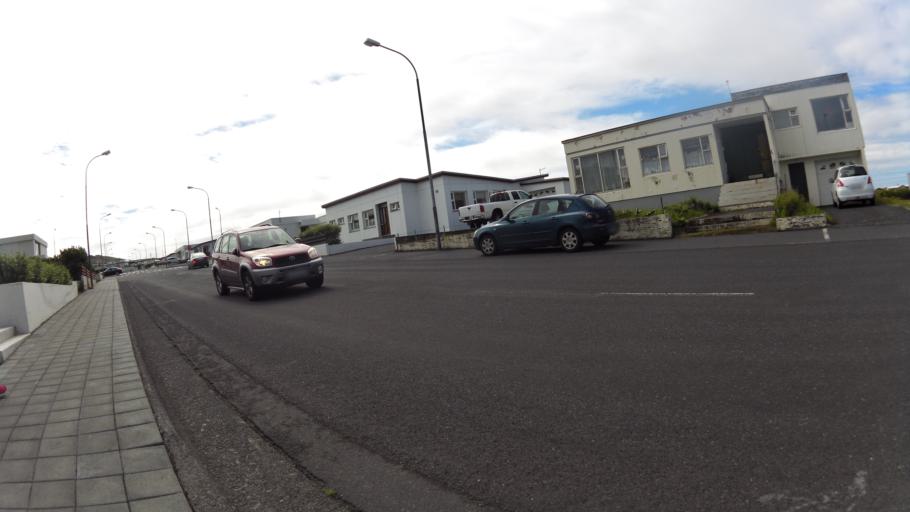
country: IS
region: South
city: Vestmannaeyjar
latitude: 63.4369
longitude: -20.2816
